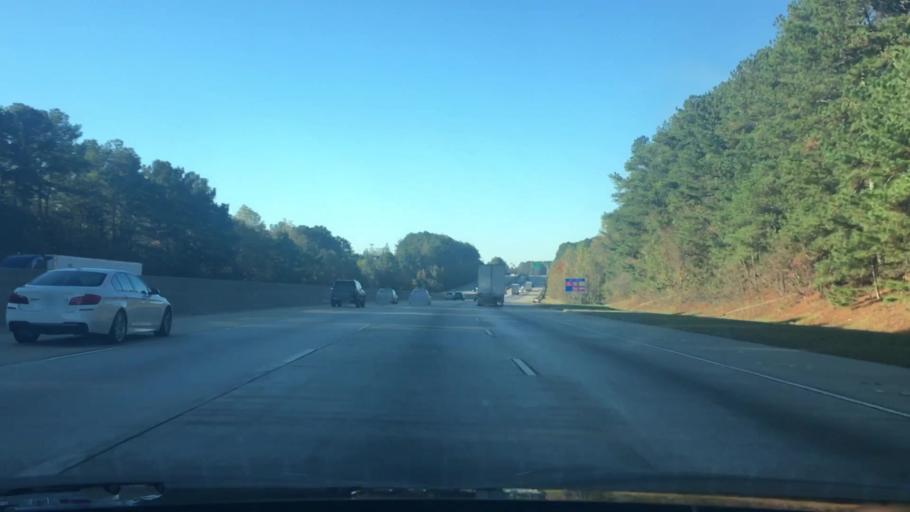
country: US
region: Georgia
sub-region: Fulton County
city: Palmetto
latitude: 33.4544
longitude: -84.6793
